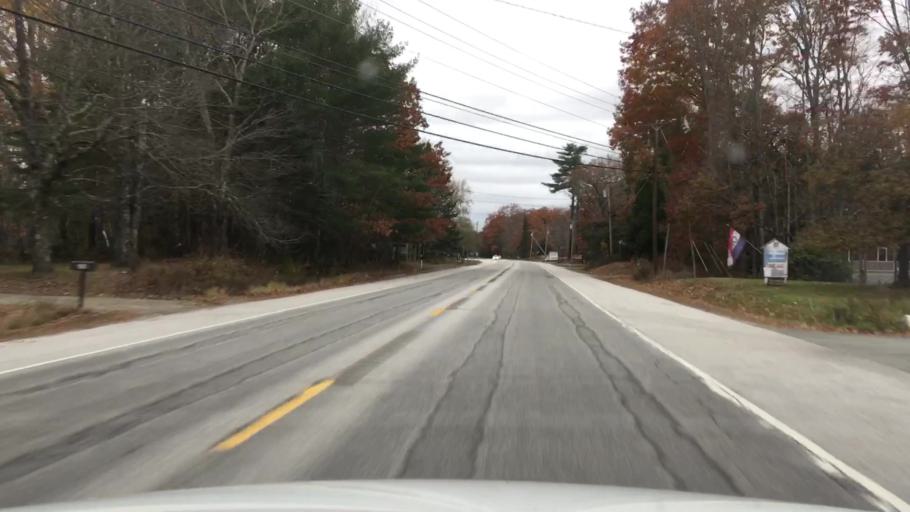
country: US
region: Maine
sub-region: Hancock County
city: Orland
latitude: 44.5644
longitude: -68.7156
